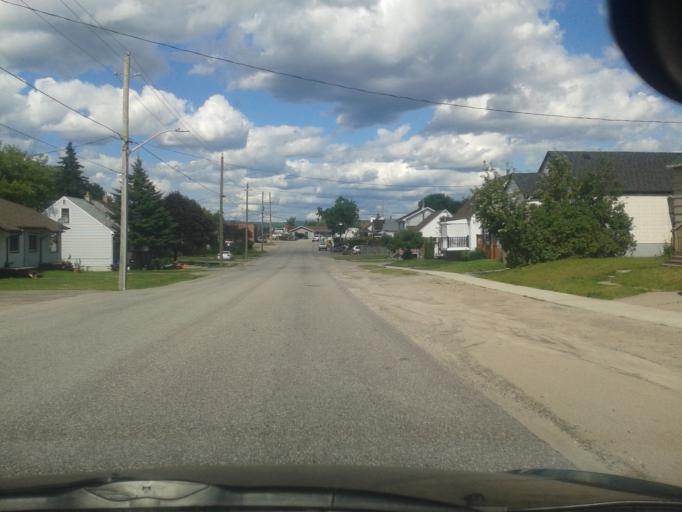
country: CA
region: Ontario
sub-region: Nipissing District
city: North Bay
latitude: 46.3087
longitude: -79.4474
